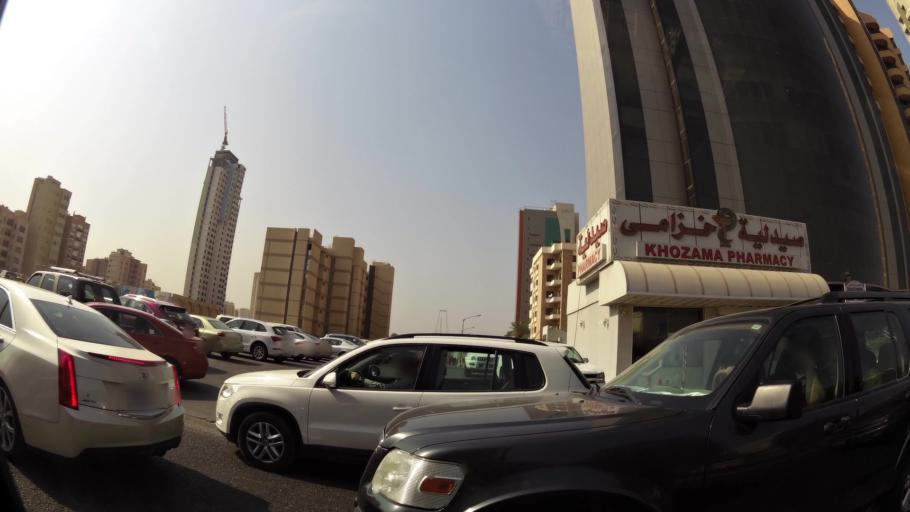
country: KW
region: Muhafazat Hawalli
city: Hawalli
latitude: 29.3392
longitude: 48.0478
